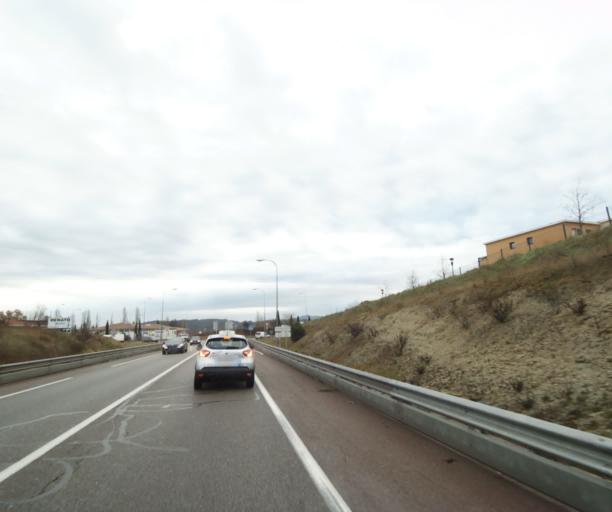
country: FR
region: Provence-Alpes-Cote d'Azur
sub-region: Departement du Var
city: Brignoles
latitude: 43.4147
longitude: 6.0675
